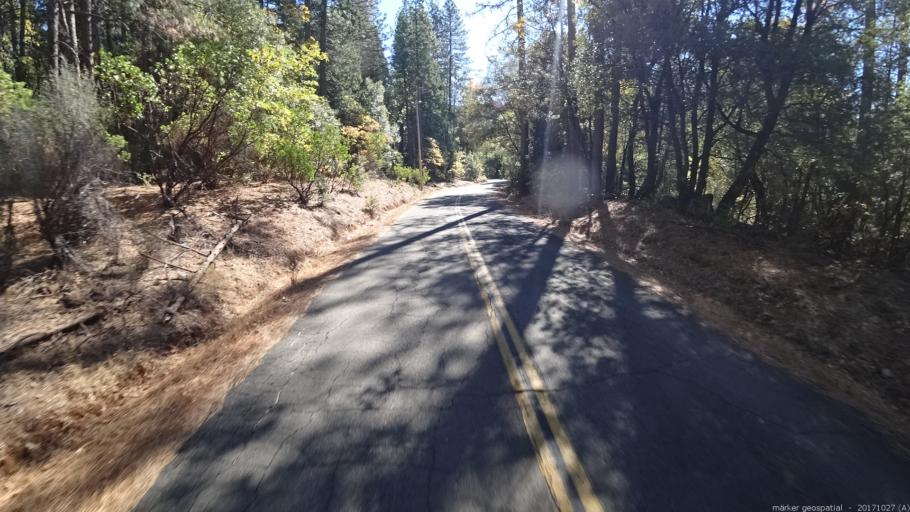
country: US
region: California
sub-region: Shasta County
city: Shingletown
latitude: 40.7509
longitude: -121.9493
